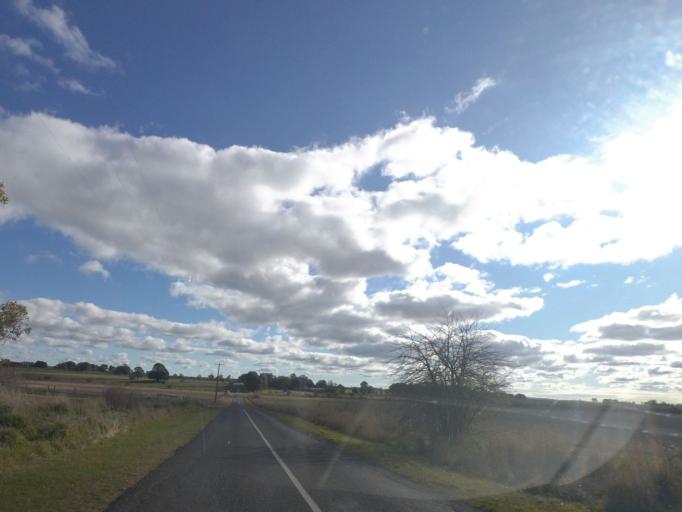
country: AU
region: Victoria
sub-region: Mount Alexander
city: Castlemaine
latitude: -37.2523
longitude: 144.4101
